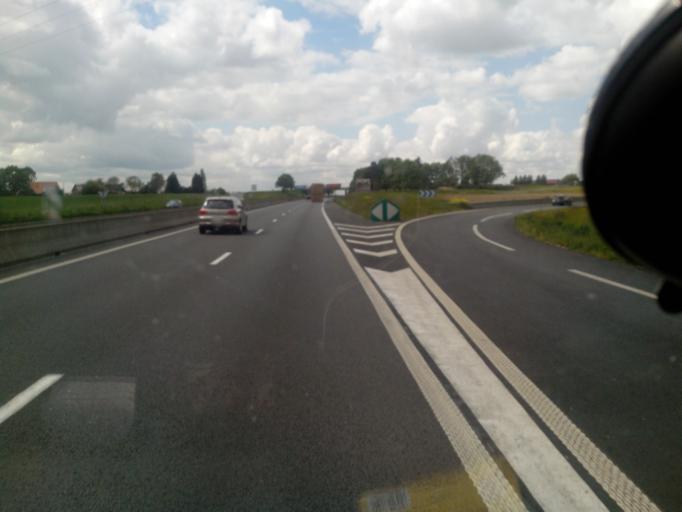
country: FR
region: Nord-Pas-de-Calais
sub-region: Departement du Nord
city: Meteren
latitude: 50.7319
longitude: 2.7011
